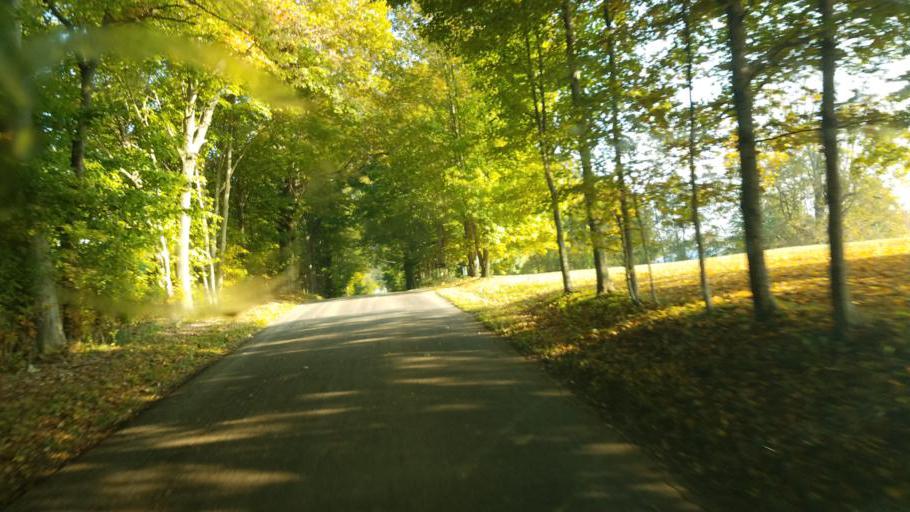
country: US
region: Ohio
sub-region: Knox County
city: Fredericktown
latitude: 40.4818
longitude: -82.5766
